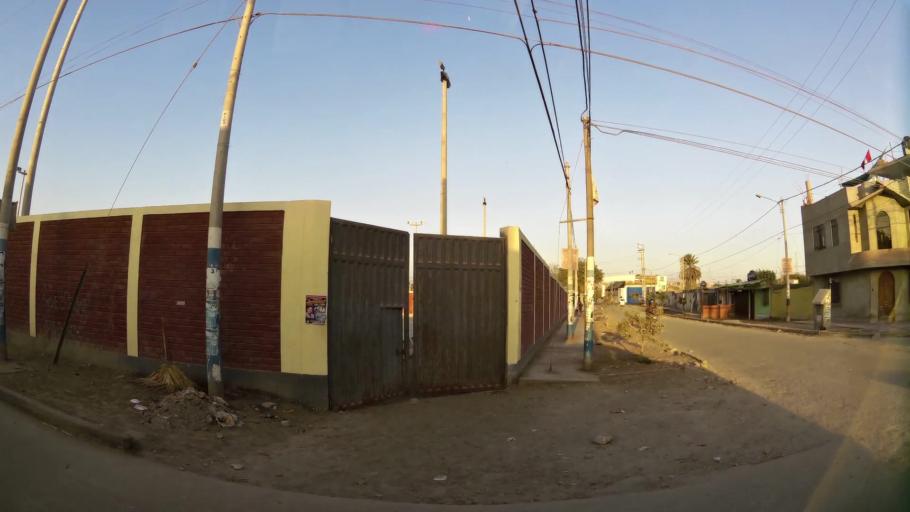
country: PE
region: Ica
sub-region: Provincia de Pisco
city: Villa Tupac Amaru
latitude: -13.7031
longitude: -76.1517
